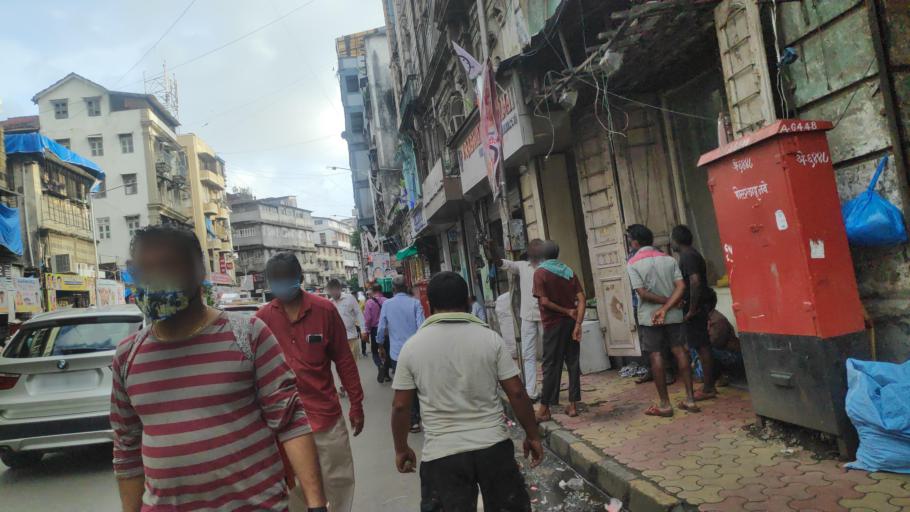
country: IN
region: Maharashtra
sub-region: Raigarh
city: Uran
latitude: 18.9496
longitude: 72.8288
